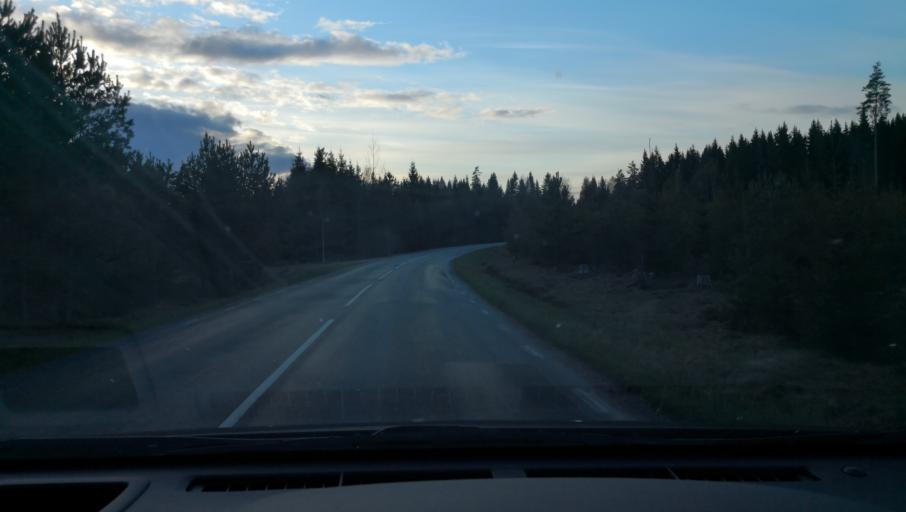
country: SE
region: OErebro
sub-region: Askersunds Kommun
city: Asbro
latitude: 58.9010
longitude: 15.1033
